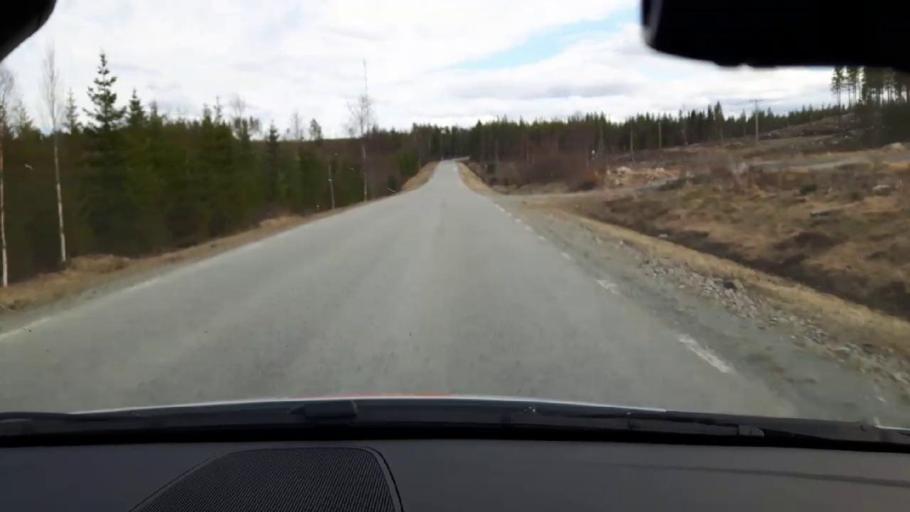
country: SE
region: Jaemtland
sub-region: Bergs Kommun
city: Hoverberg
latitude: 62.7076
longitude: 14.6149
